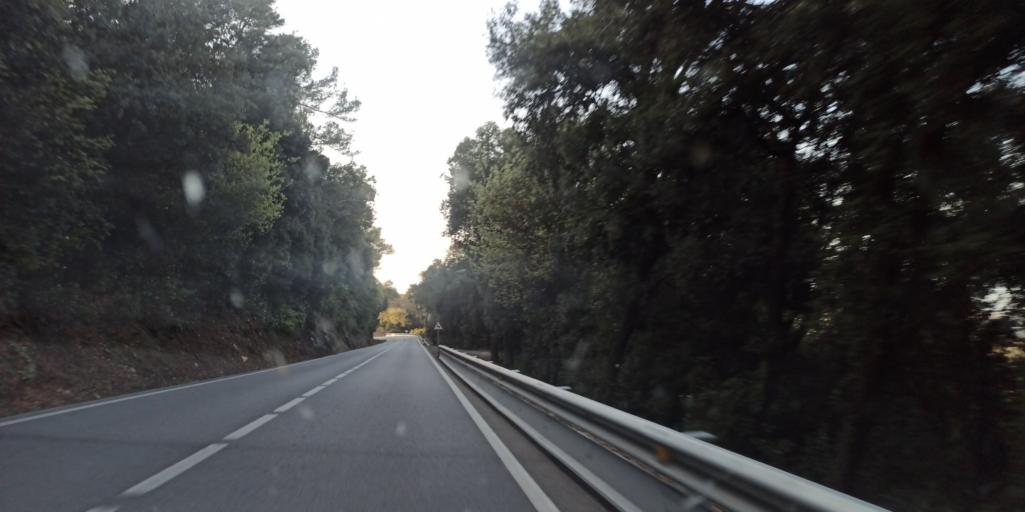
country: ES
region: Catalonia
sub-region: Provincia de Barcelona
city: Sant Cugat del Valles
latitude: 41.4400
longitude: 2.1000
